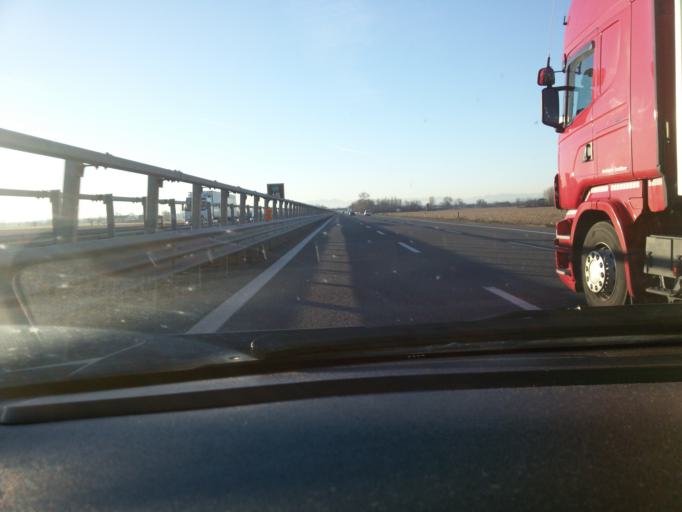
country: IT
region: Piedmont
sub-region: Provincia di Alessandria
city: Castelletto Monferrato
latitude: 44.9581
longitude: 8.5578
